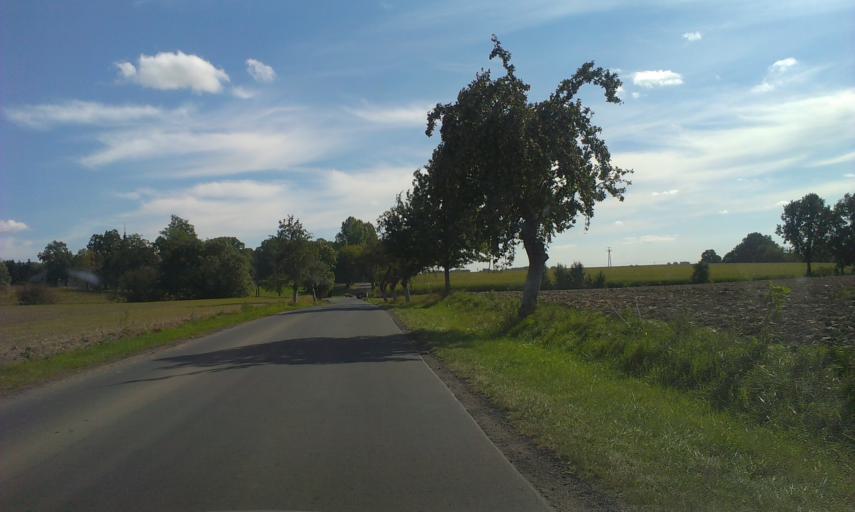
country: PL
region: Greater Poland Voivodeship
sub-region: Powiat pilski
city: Lobzenica
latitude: 53.2718
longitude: 17.2324
